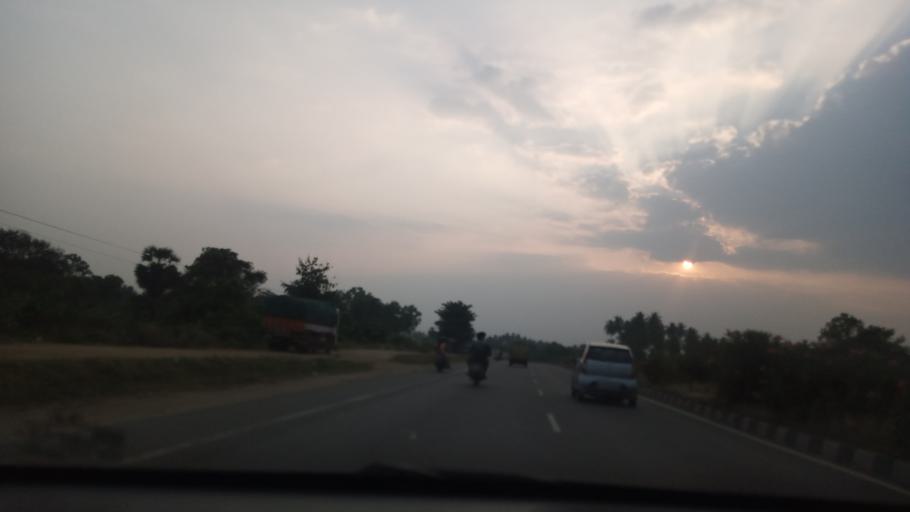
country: IN
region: Tamil Nadu
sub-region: Erode
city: Perundurai
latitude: 11.3156
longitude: 77.6158
